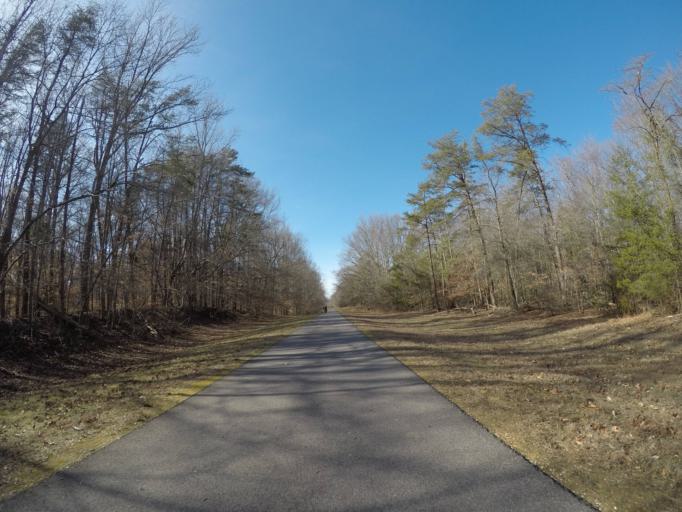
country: US
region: Maryland
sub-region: Charles County
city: Bennsville
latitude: 38.5961
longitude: -76.9873
